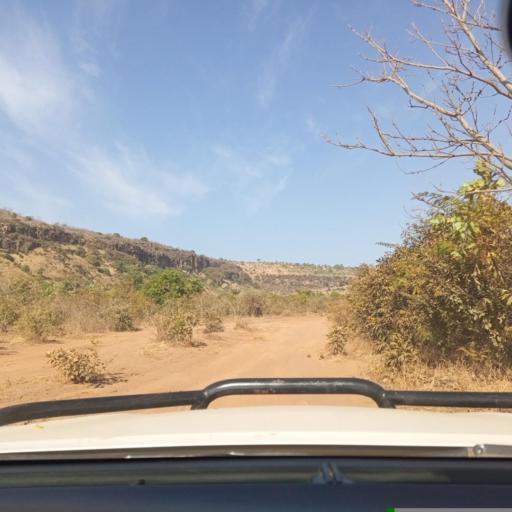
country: ML
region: Bamako
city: Bamako
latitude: 12.5574
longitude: -8.1500
